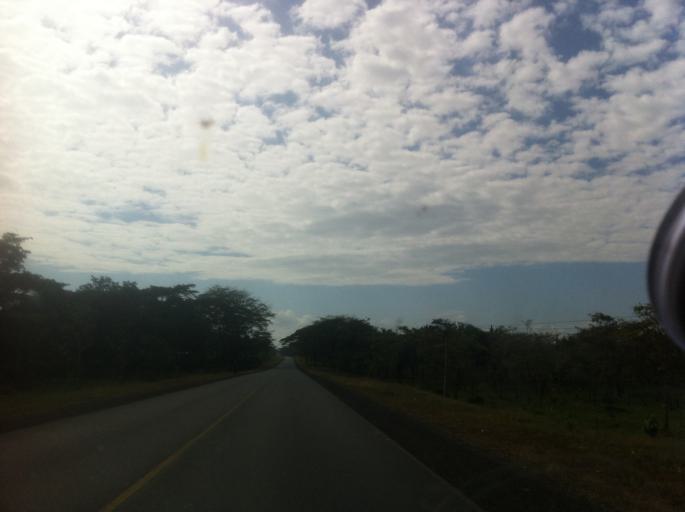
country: NI
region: Rio San Juan
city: San Miguelito
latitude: 11.3513
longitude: -84.7595
